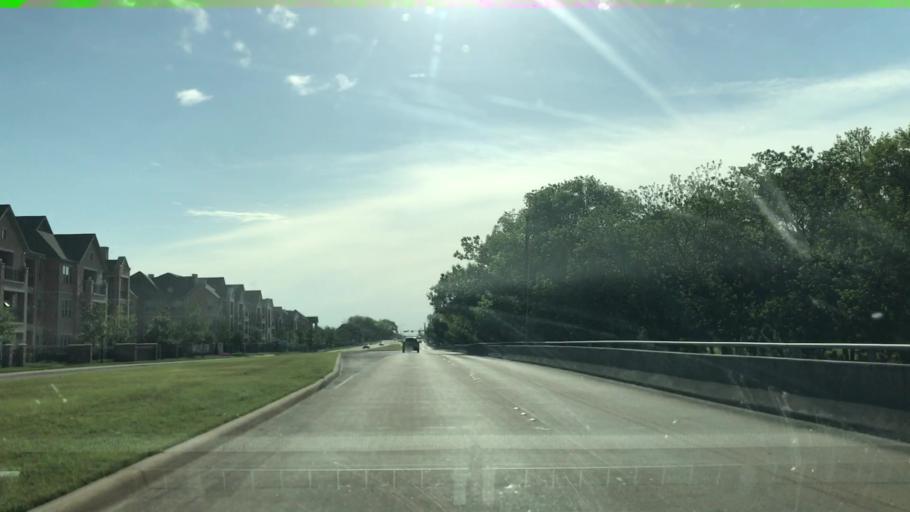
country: US
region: Texas
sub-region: Dallas County
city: Farmers Branch
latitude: 32.8955
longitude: -96.9227
